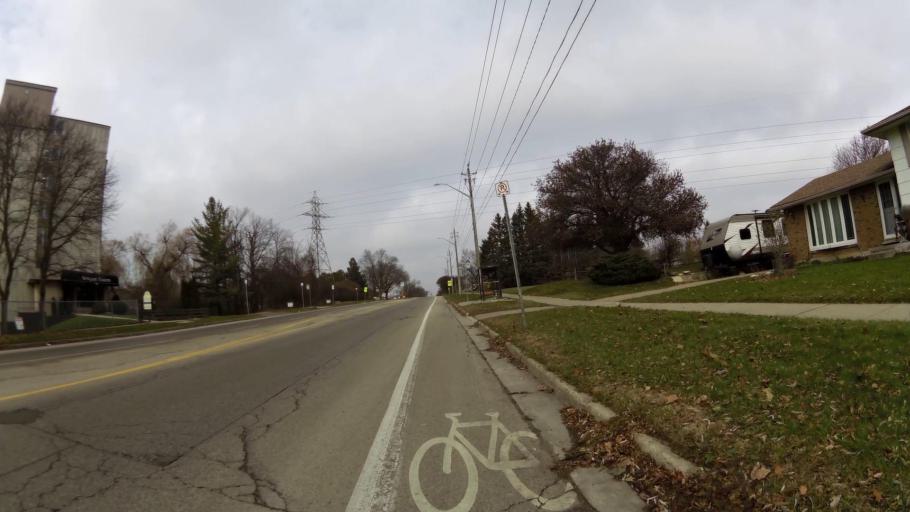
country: CA
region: Ontario
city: Kitchener
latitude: 43.4183
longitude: -80.4826
